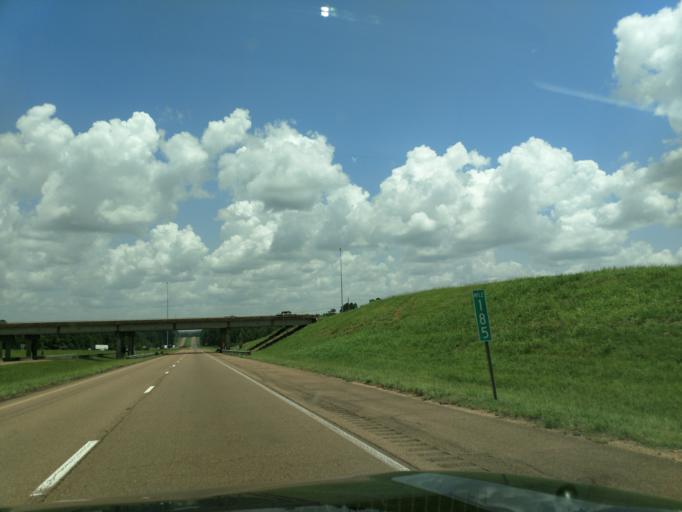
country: US
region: Mississippi
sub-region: Montgomery County
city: Winona
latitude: 33.4855
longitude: -89.7643
